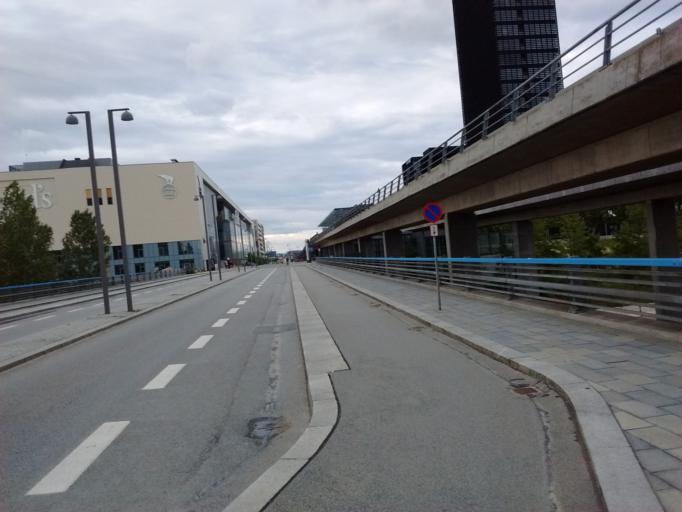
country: DK
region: Capital Region
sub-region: Tarnby Kommune
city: Tarnby
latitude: 55.6277
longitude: 12.5786
